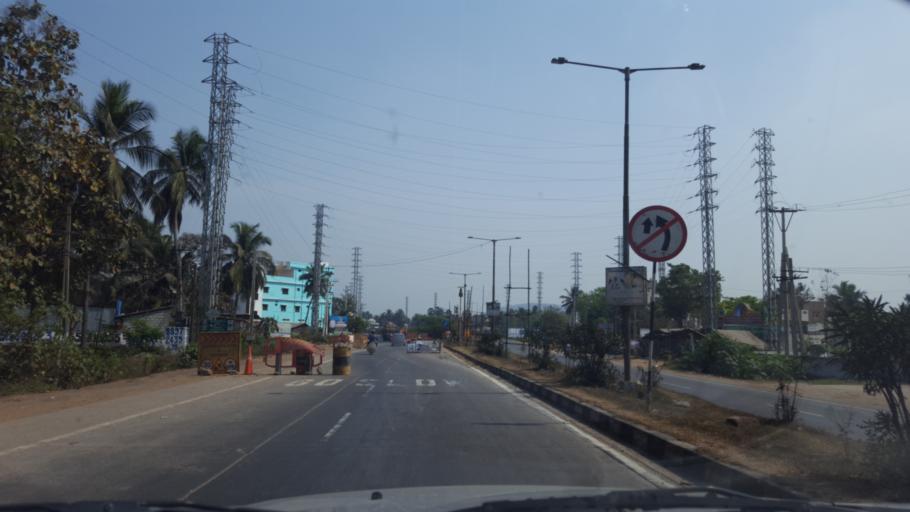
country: IN
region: Andhra Pradesh
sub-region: Vishakhapatnam
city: Anakapalle
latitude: 17.6769
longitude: 82.9954
